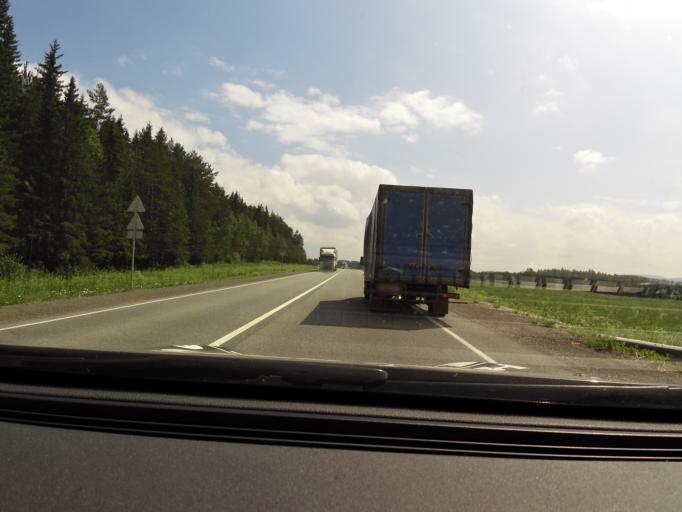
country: RU
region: Perm
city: Suksun
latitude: 57.0372
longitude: 57.4453
